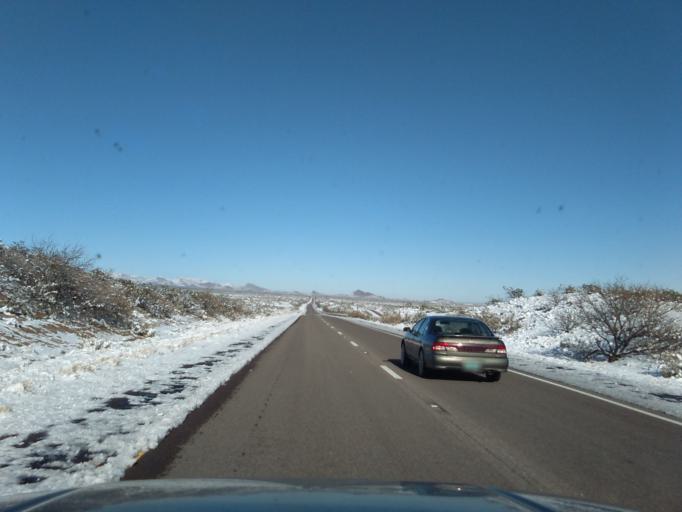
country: US
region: New Mexico
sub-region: Socorro County
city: Socorro
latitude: 33.6826
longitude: -107.0685
